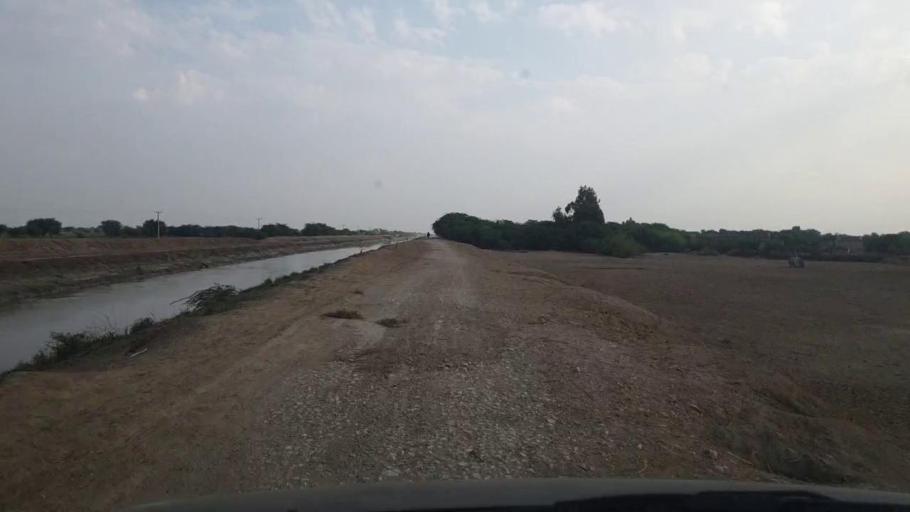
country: PK
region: Sindh
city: Badin
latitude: 24.5257
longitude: 68.6803
